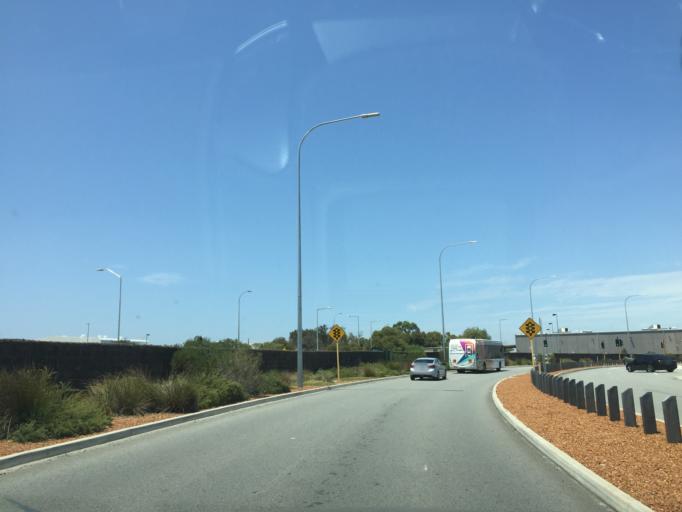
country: AU
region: Western Australia
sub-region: Belmont
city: Redcliffe
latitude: -31.9433
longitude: 115.9767
